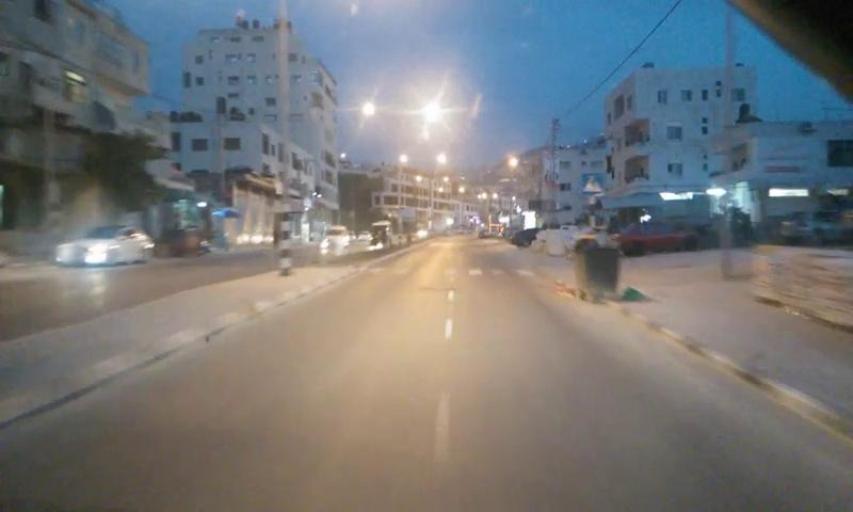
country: PS
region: West Bank
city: Zawata
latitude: 32.2387
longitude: 35.2324
